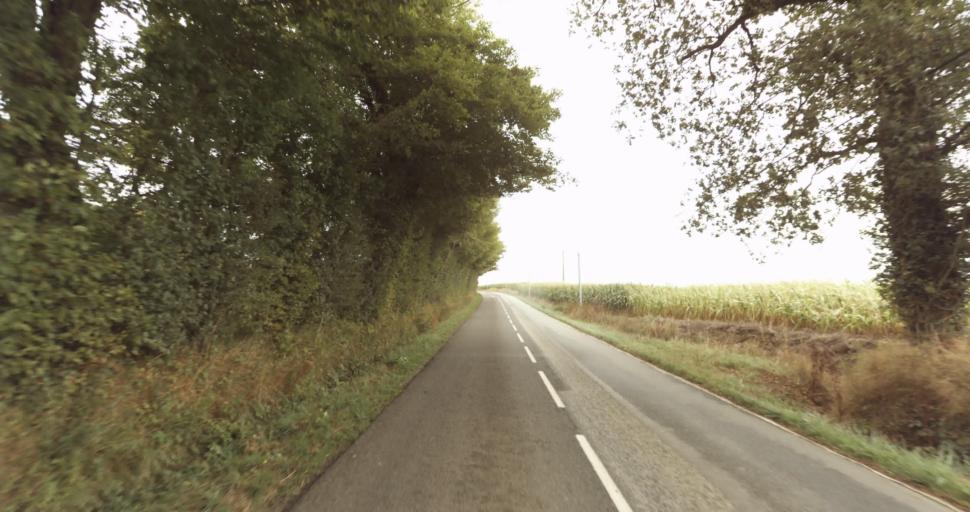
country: FR
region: Lower Normandy
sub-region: Departement de l'Orne
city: Gace
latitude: 48.7062
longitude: 0.3039
